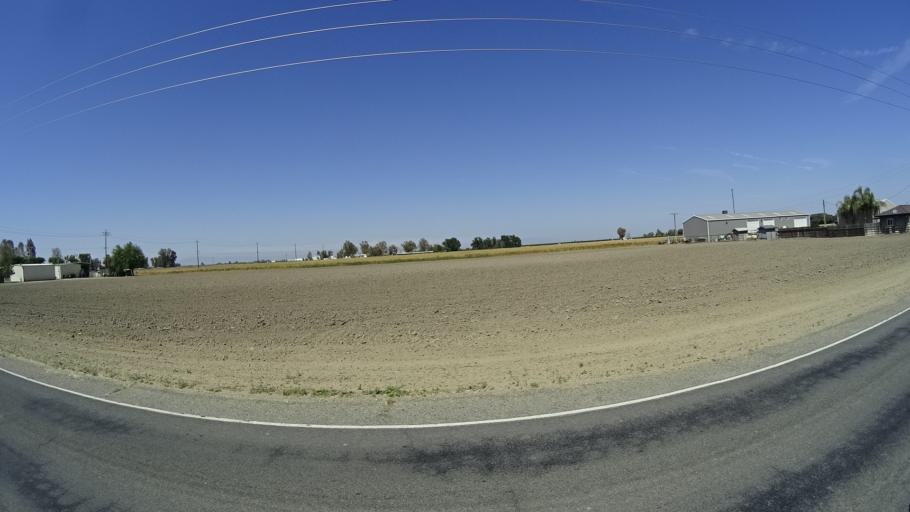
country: US
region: California
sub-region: Kings County
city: Stratford
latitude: 36.2271
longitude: -119.7804
